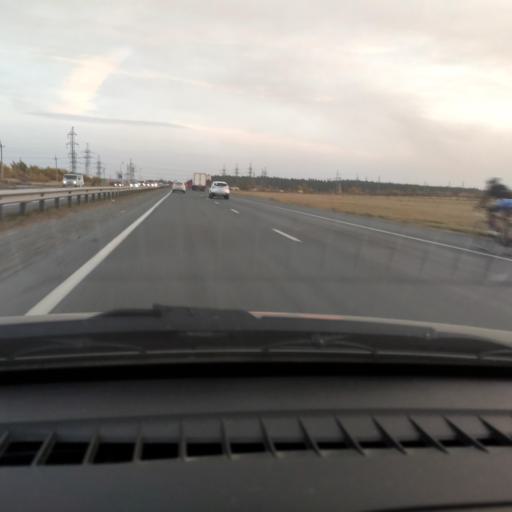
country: RU
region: Samara
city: Zhigulevsk
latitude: 53.5479
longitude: 49.5095
